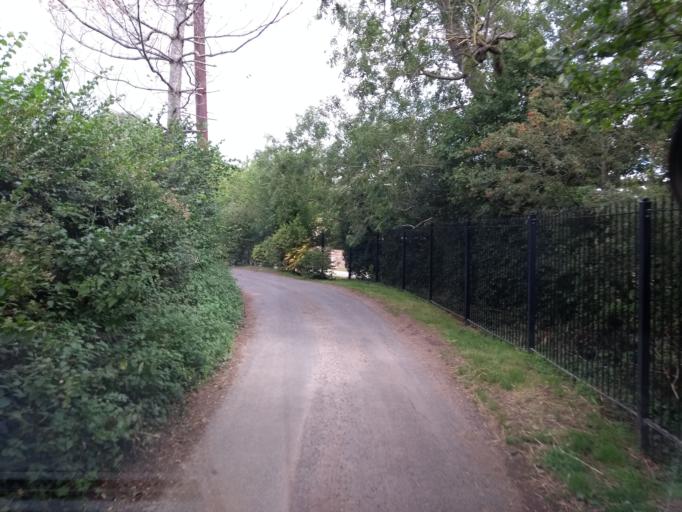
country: GB
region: England
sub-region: Somerset
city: Creech Saint Michael
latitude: 51.0353
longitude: -3.0133
